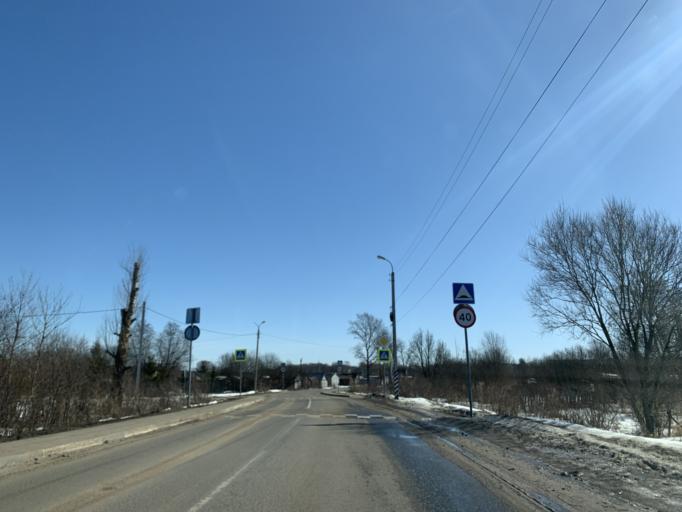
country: RU
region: Jaroslavl
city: Konstantinovskiy
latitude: 57.8366
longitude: 39.5863
